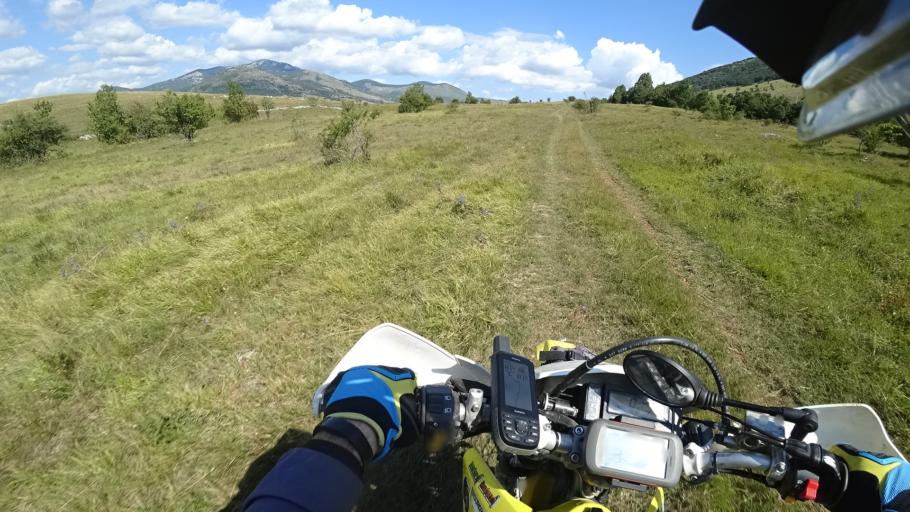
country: HR
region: Zadarska
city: Gracac
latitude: 44.4142
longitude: 15.9271
